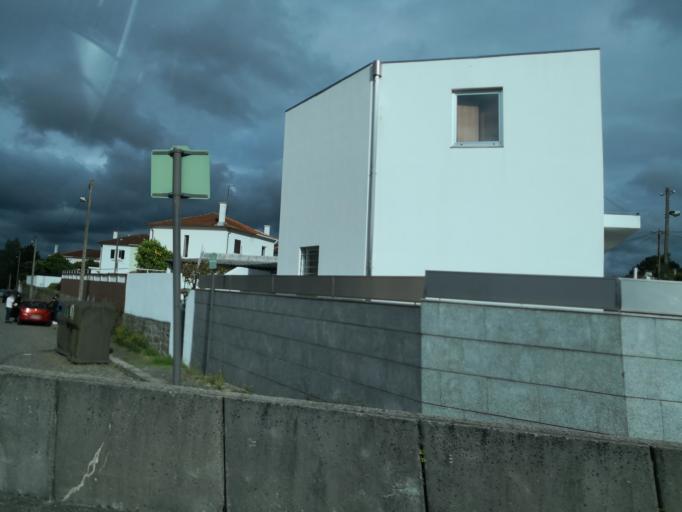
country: PT
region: Porto
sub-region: Gondomar
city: Rio Tinto
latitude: 41.1682
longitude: -8.5742
